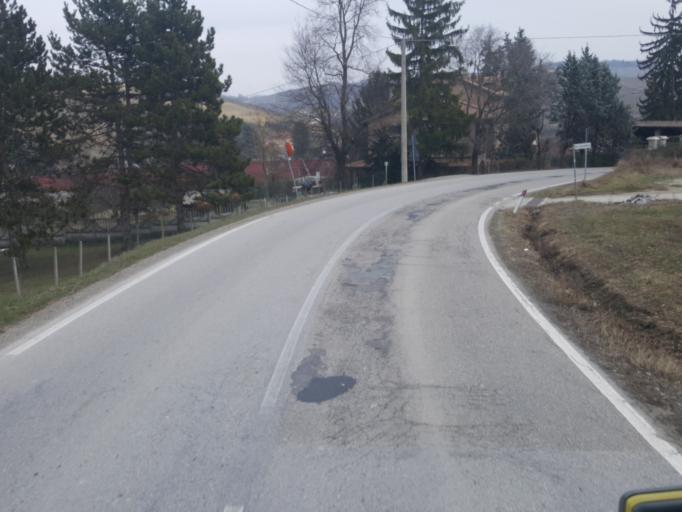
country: IT
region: Piedmont
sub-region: Provincia di Asti
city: Castelnuovo Belbo
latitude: 44.7764
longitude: 8.3973
